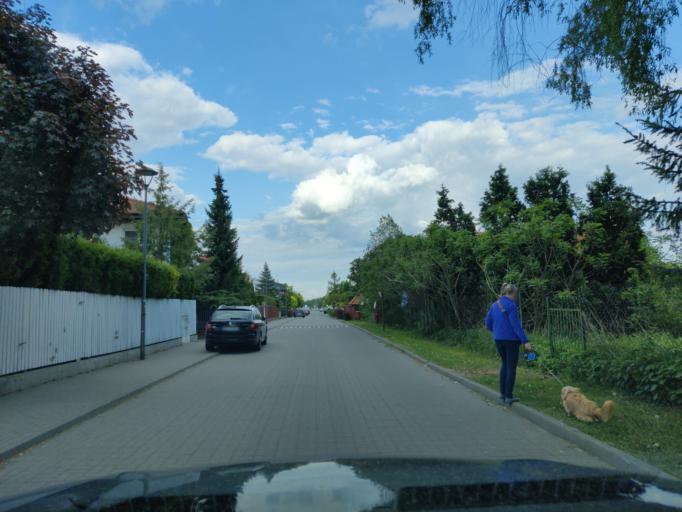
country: PL
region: Masovian Voivodeship
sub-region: Warszawa
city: Kabaty
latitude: 52.1277
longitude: 21.0927
